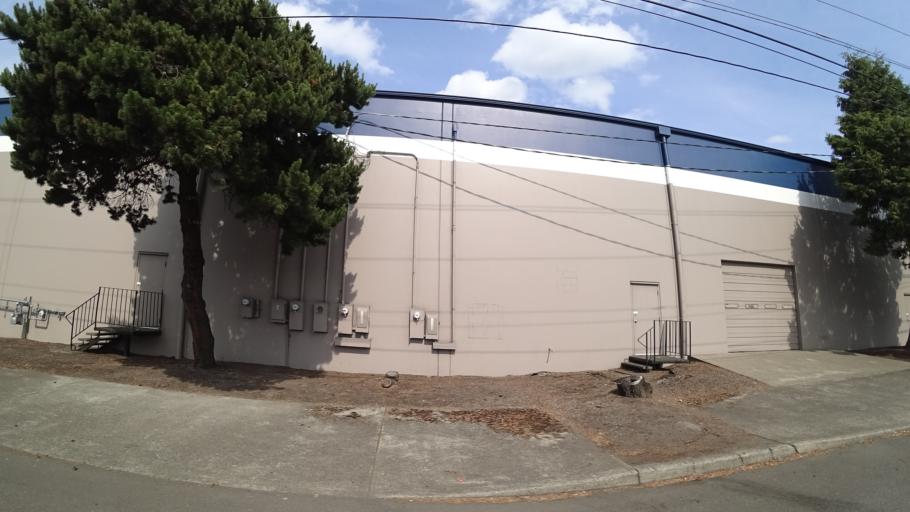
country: US
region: Washington
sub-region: Clark County
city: Vancouver
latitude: 45.5787
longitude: -122.6439
